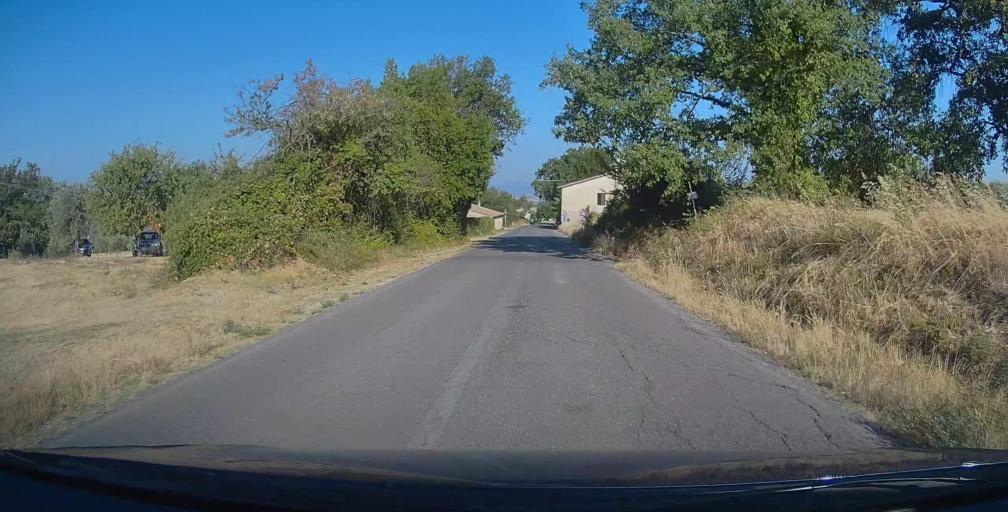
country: IT
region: Umbria
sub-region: Provincia di Terni
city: Calvi dell'Umbria
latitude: 42.4135
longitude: 12.5493
